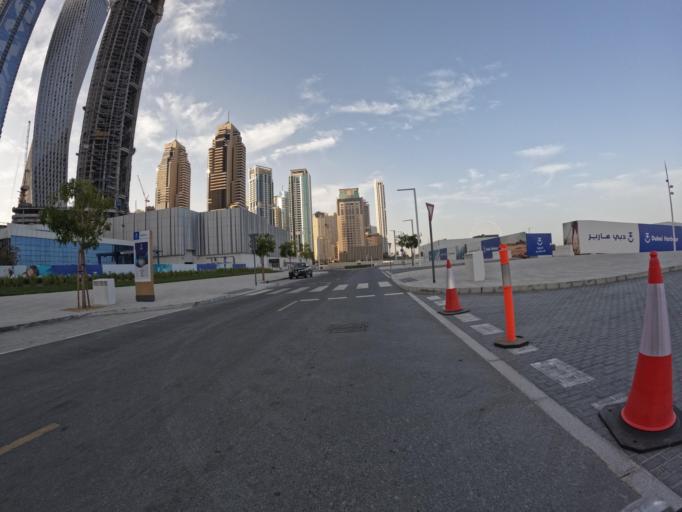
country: AE
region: Dubai
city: Dubai
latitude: 25.0890
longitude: 55.1443
